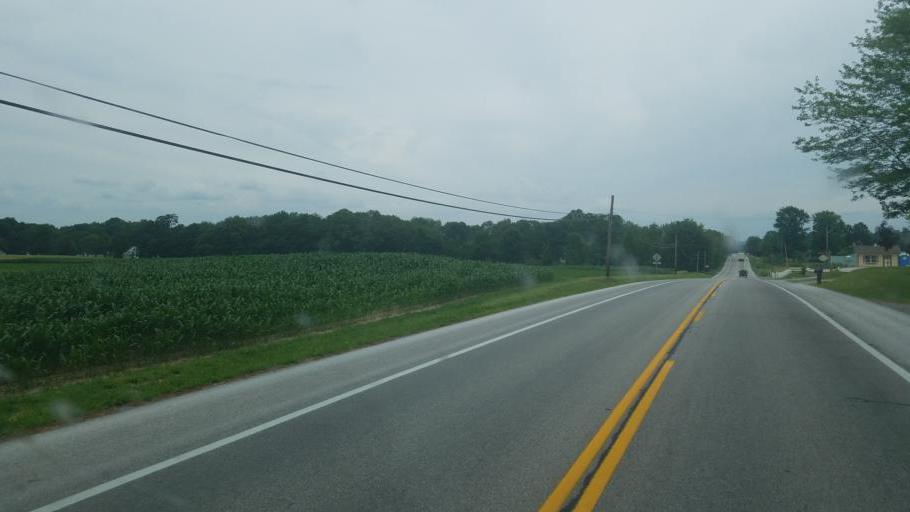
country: US
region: Ohio
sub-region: Geauga County
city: Middlefield
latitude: 41.4585
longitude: -80.9738
